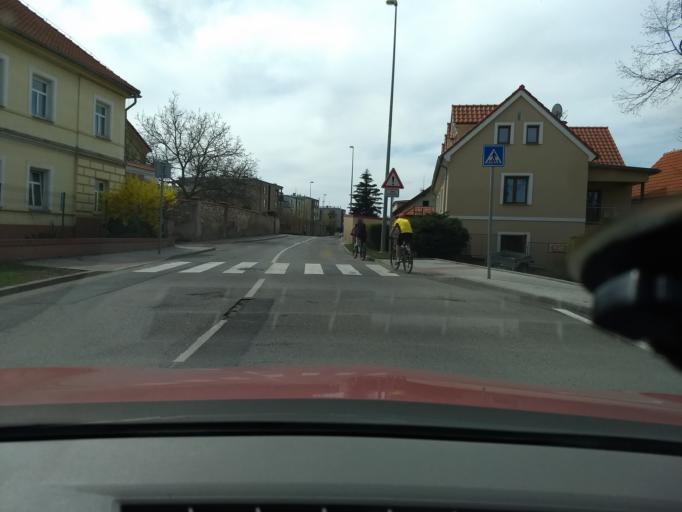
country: CZ
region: Central Bohemia
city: Hostivice
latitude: 50.0623
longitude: 14.2824
